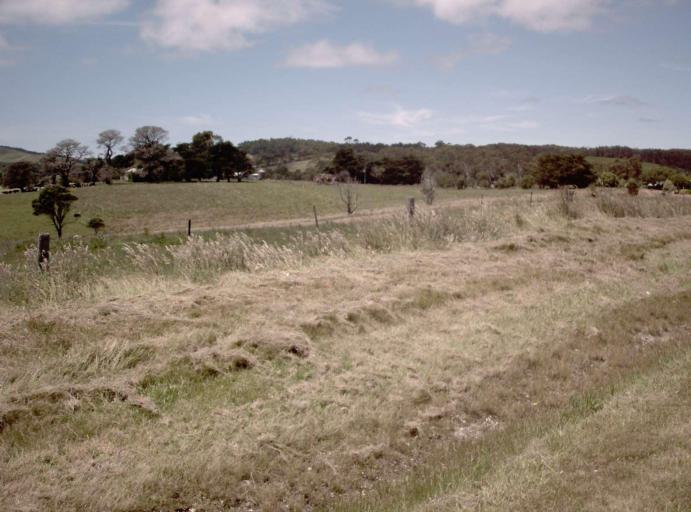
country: AU
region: Victoria
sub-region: Bass Coast
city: North Wonthaggi
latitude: -38.7134
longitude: 146.0991
